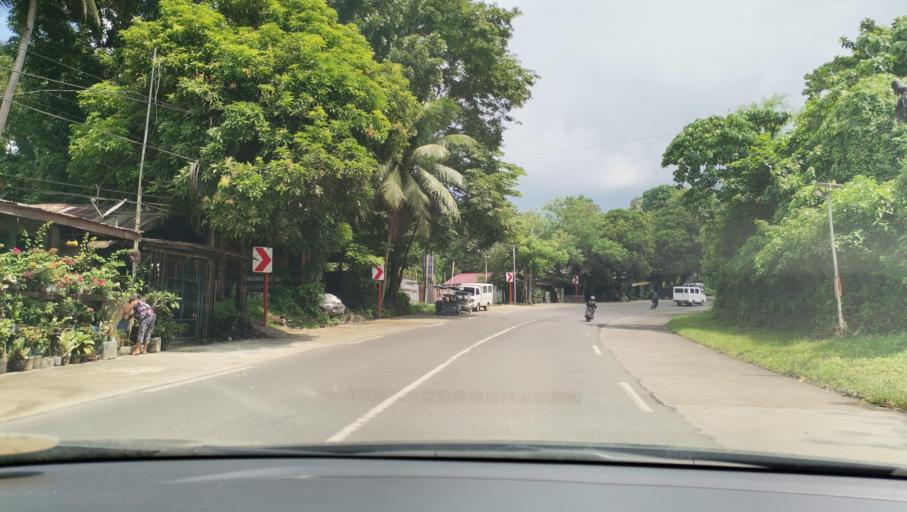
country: PH
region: Calabarzon
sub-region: Province of Quezon
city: Calauag
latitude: 13.9536
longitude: 122.2887
